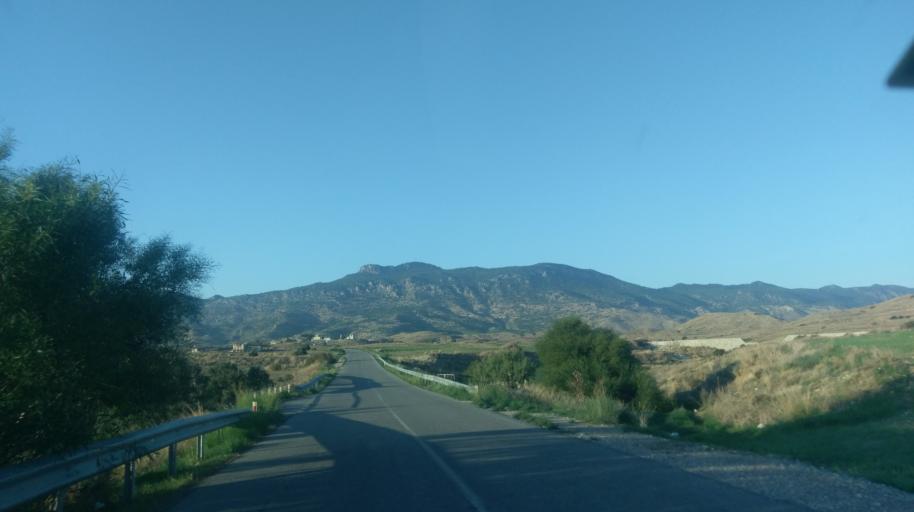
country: CY
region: Ammochostos
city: Lefkonoiko
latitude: 35.2453
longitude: 33.5531
